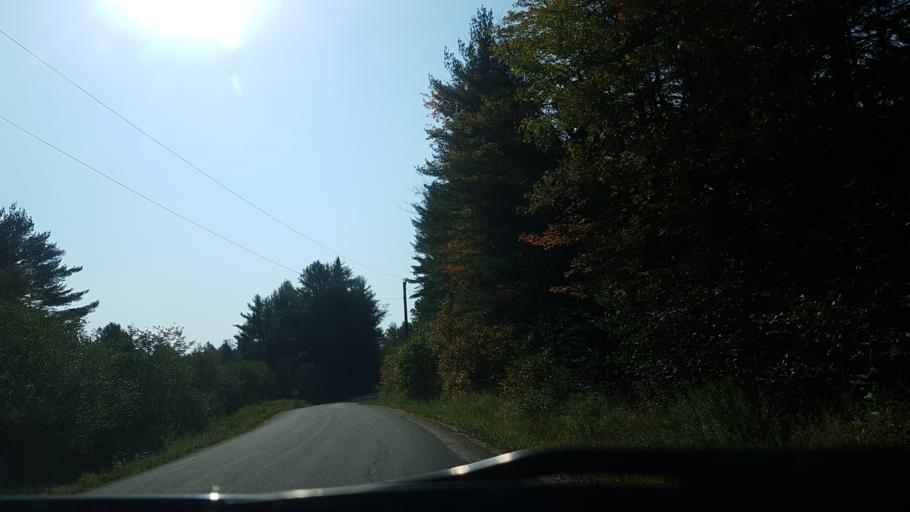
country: CA
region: Ontario
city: Bracebridge
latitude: 44.9679
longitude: -79.2553
